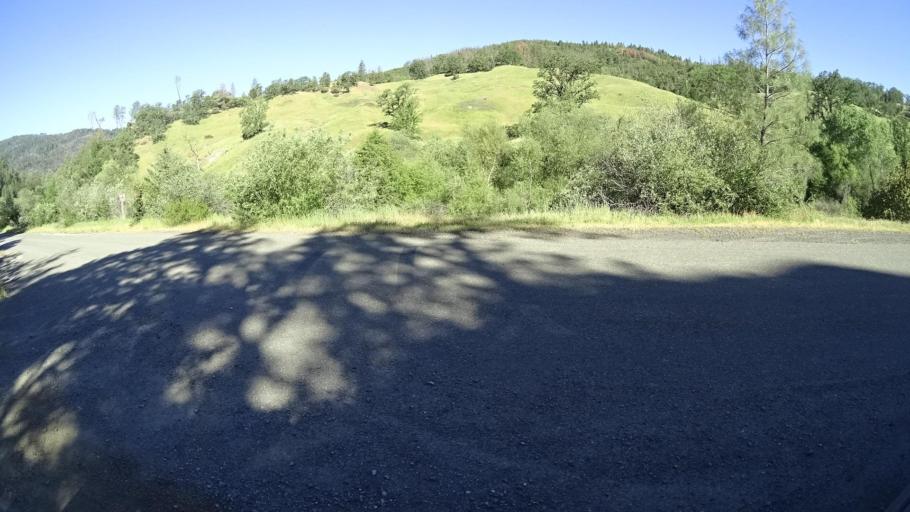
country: US
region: California
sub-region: Lake County
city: Upper Lake
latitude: 39.4096
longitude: -122.9802
